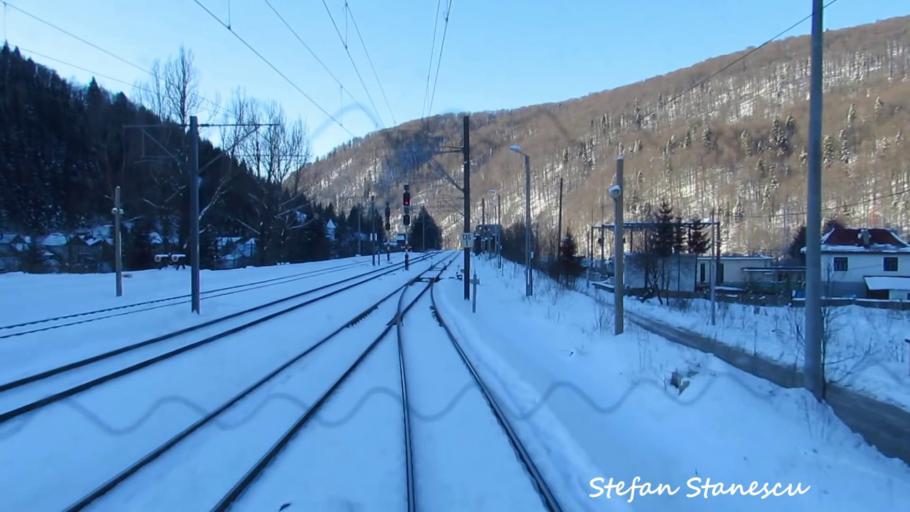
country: RO
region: Prahova
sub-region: Oras Azuga
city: Azuga
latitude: 45.4365
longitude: 25.5505
